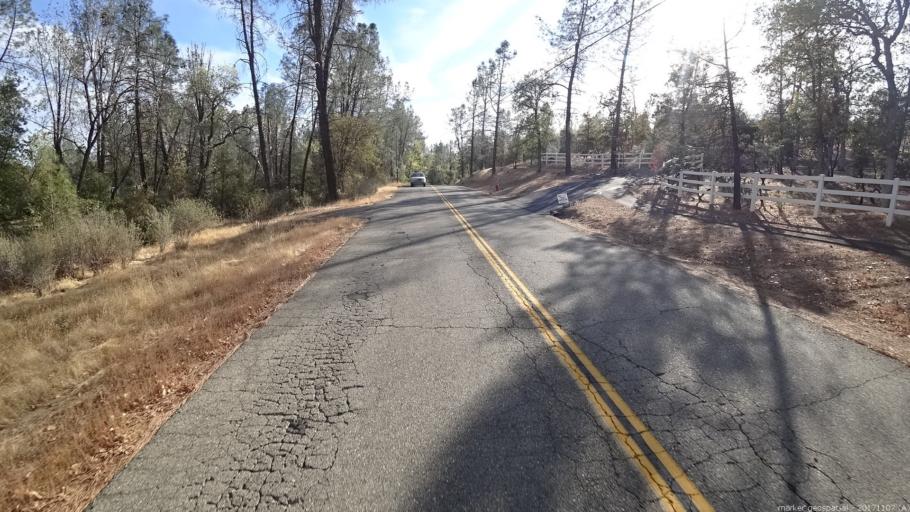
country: US
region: California
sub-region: Shasta County
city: Redding
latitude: 40.5146
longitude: -122.4402
